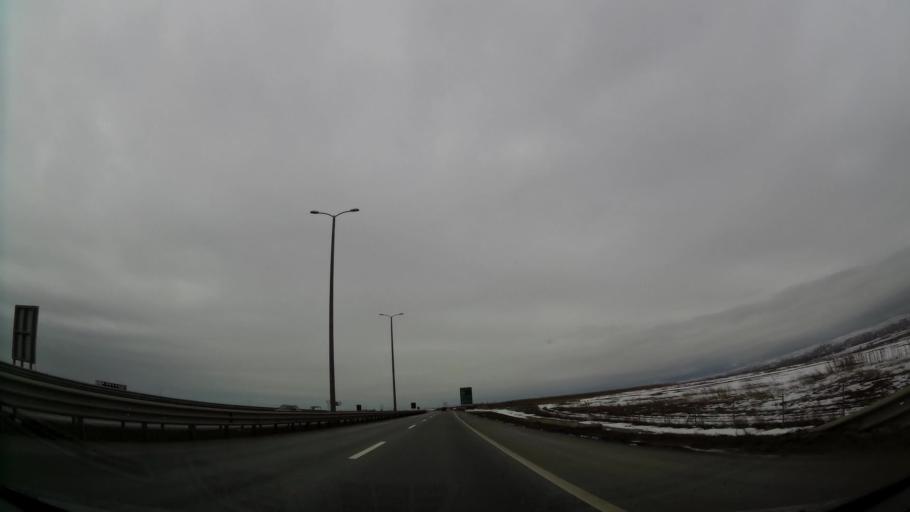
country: XK
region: Pristina
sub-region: Kosovo Polje
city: Kosovo Polje
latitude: 42.6265
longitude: 21.1315
